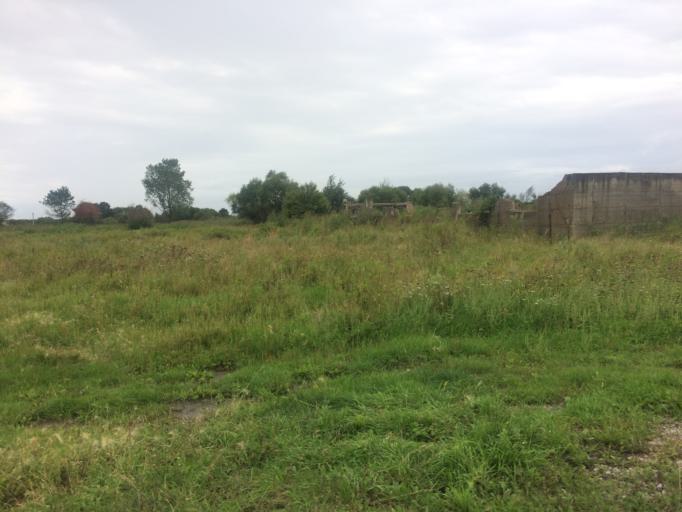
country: RU
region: Primorskiy
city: Lazo
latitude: 45.8308
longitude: 133.6122
